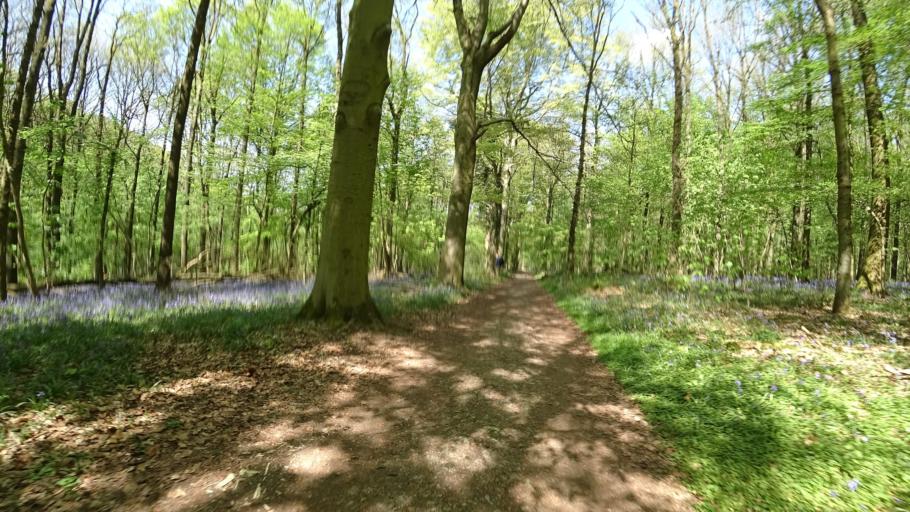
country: BE
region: Wallonia
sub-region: Province du Brabant Wallon
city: Braine-le-Chateau
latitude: 50.7043
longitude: 4.2763
